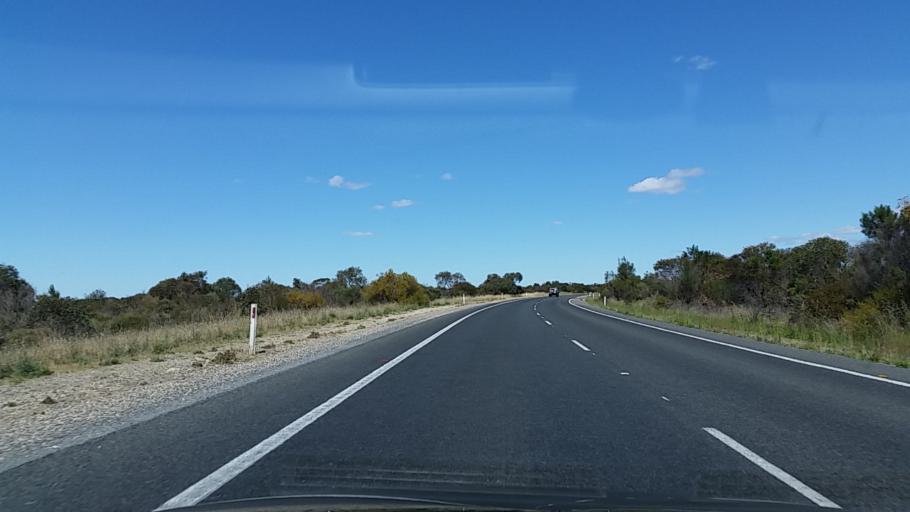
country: AU
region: South Australia
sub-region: Murray Bridge
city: Tailem Bend
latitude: -35.2061
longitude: 139.4042
